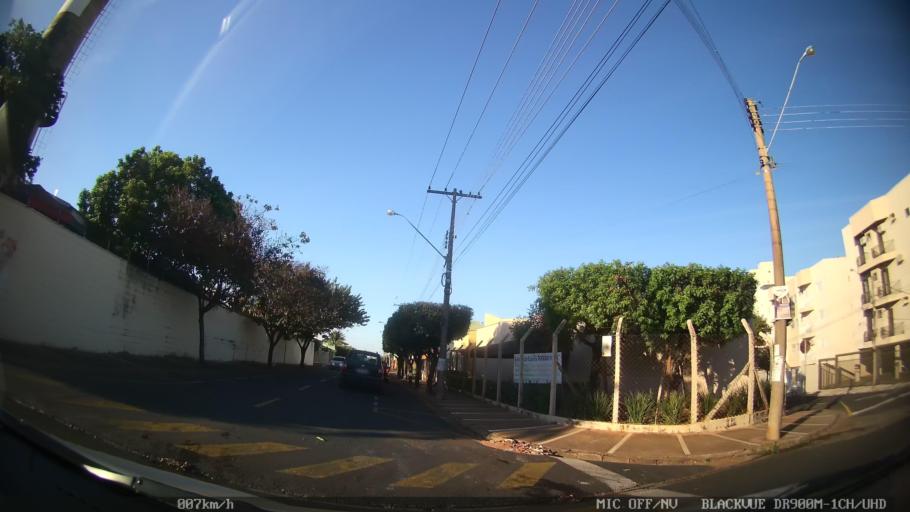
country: BR
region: Sao Paulo
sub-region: Sao Jose Do Rio Preto
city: Sao Jose do Rio Preto
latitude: -20.7980
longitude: -49.3623
